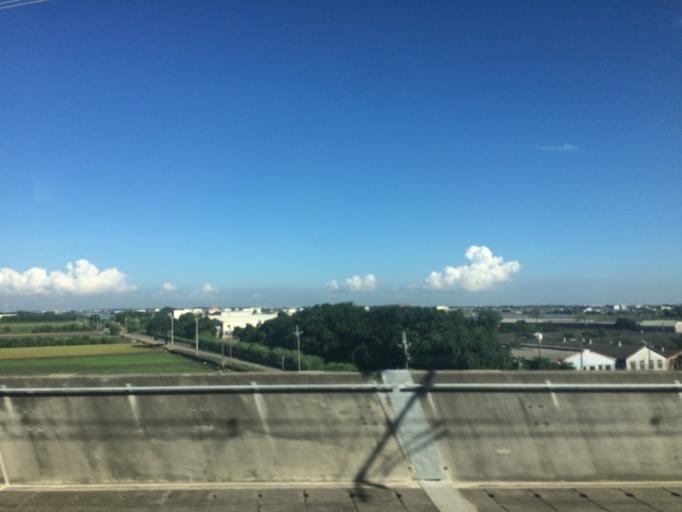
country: TW
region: Taiwan
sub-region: Yunlin
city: Douliu
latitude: 23.6725
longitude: 120.3754
